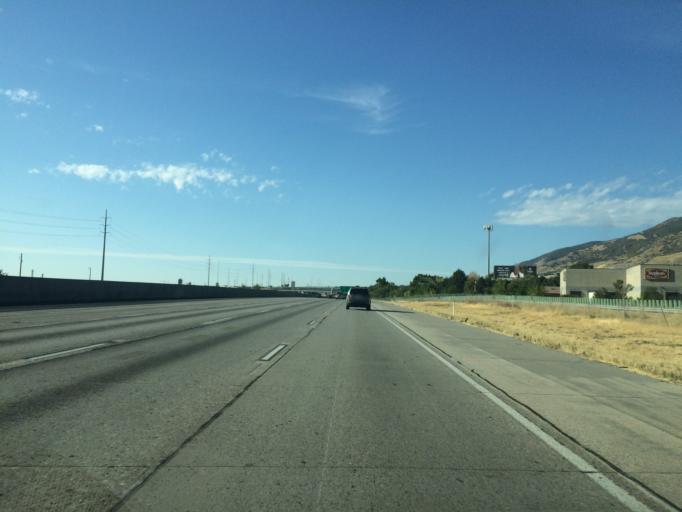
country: US
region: Utah
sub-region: Davis County
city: Farmington
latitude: 40.9743
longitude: -111.8945
